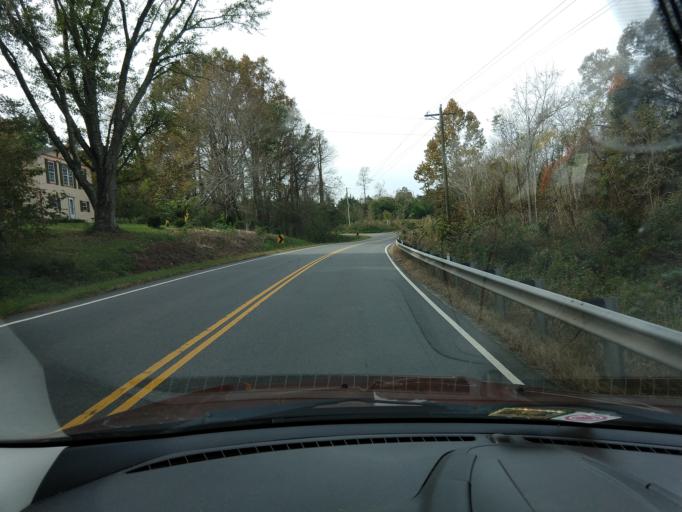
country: US
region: Virginia
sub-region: Franklin County
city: Union Hall
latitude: 36.9536
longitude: -79.5479
